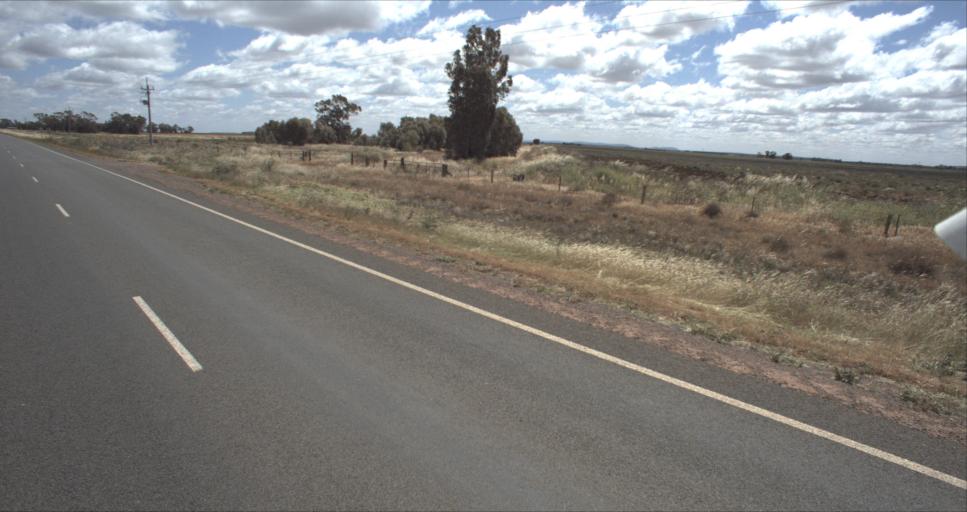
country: AU
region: New South Wales
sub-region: Murrumbidgee Shire
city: Darlington Point
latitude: -34.4879
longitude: 146.1615
